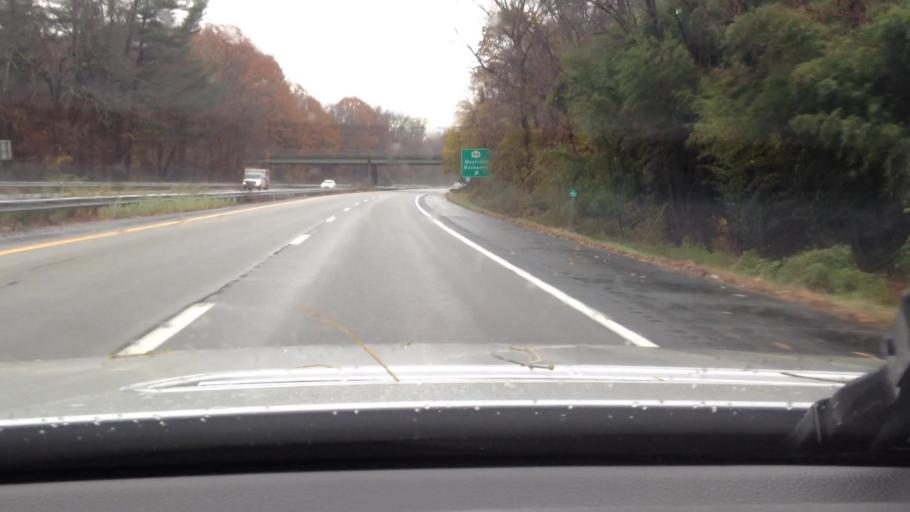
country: US
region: New York
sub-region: Westchester County
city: Crugers
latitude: 41.2377
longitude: -73.9139
